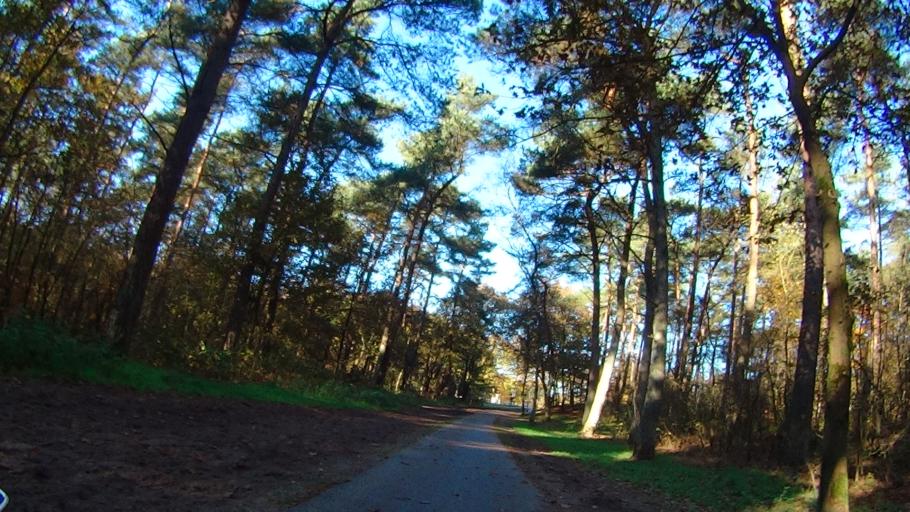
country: NL
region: Utrecht
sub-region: Gemeente Soest
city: Soest
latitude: 52.1550
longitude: 5.2859
